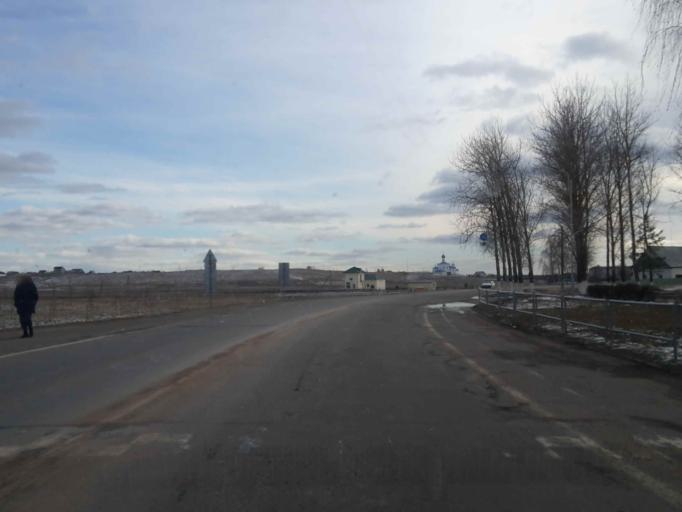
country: BY
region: Minsk
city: Myadzyel
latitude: 54.8760
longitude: 26.9414
